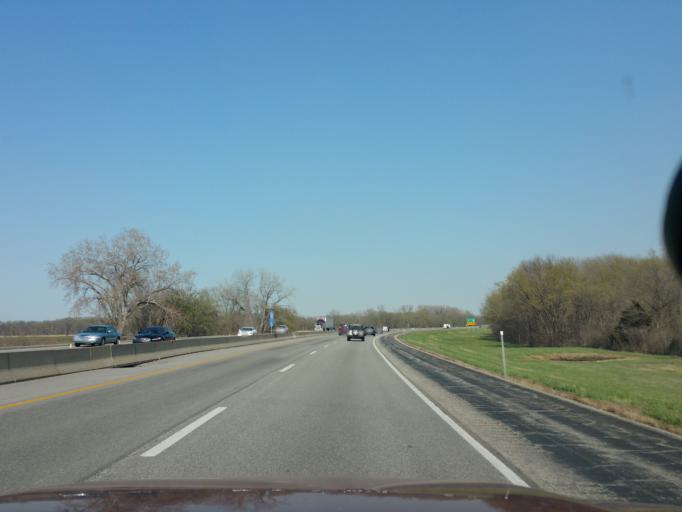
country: US
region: Kansas
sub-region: Leavenworth County
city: Tonganoxie
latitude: 39.0666
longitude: -95.0343
